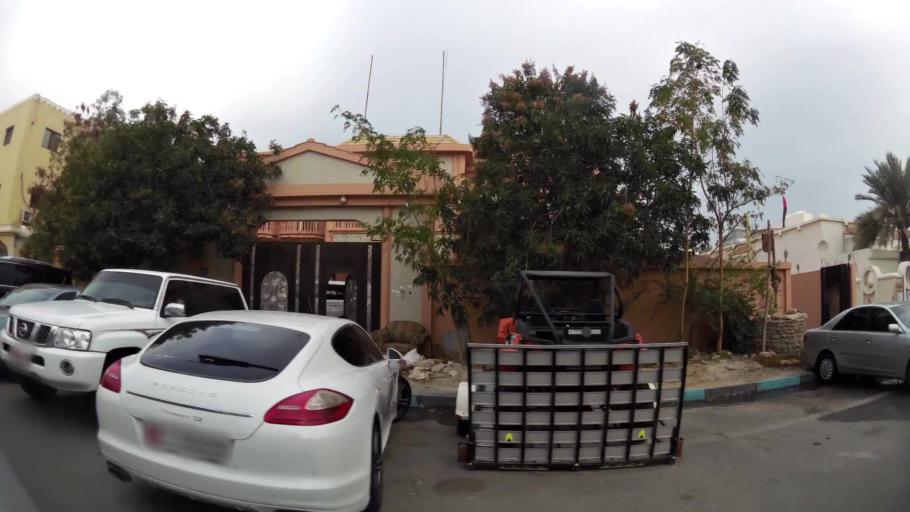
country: AE
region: Abu Dhabi
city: Abu Dhabi
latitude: 24.4853
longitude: 54.3682
